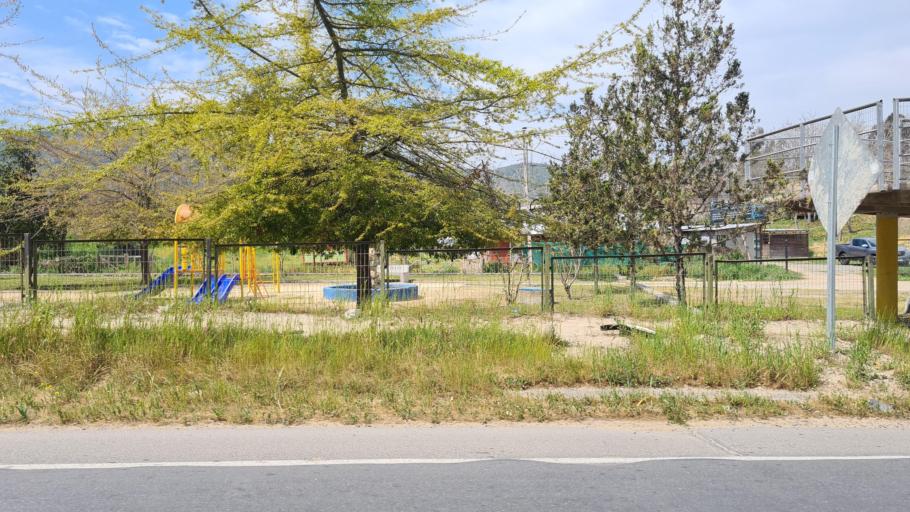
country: CL
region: O'Higgins
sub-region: Provincia de Cachapoal
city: San Vicente
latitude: -34.1788
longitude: -71.3994
